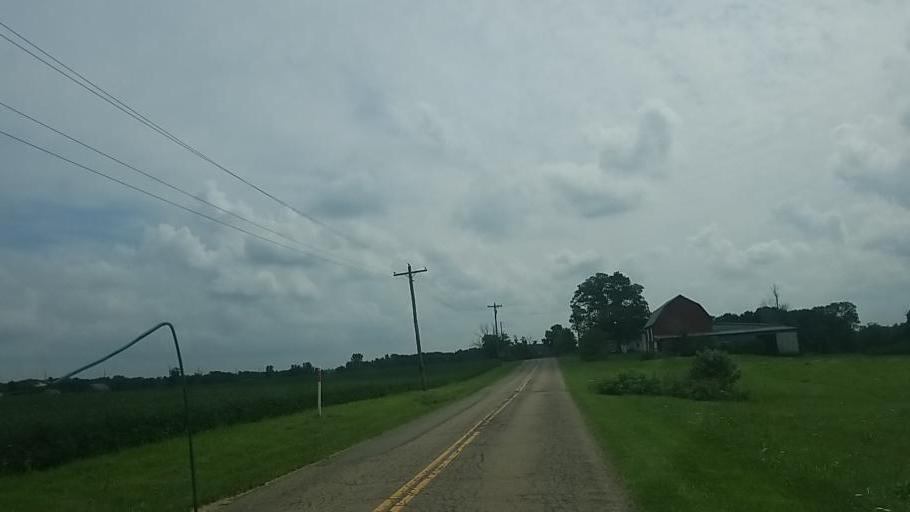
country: US
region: Ohio
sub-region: Knox County
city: Mount Vernon
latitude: 40.3190
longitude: -82.4754
